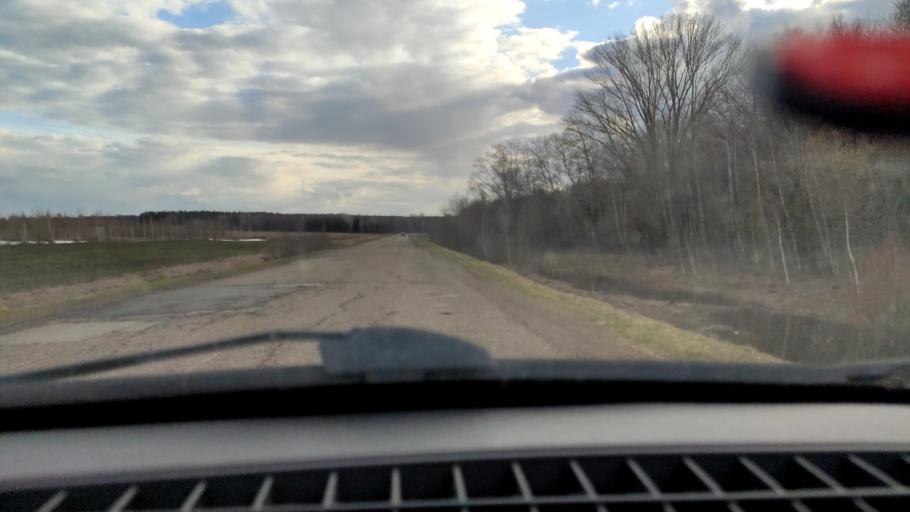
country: RU
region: Bashkortostan
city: Karmaskaly
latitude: 54.3229
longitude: 55.9846
